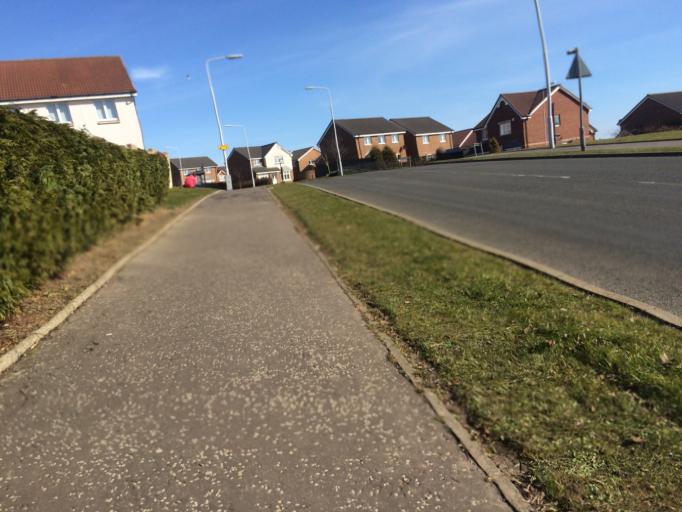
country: GB
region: Scotland
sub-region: Fife
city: Kirkcaldy
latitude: 56.1351
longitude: -3.1931
